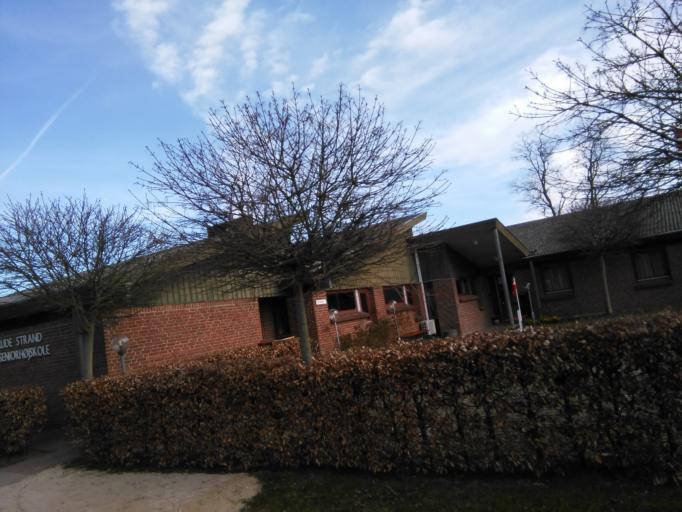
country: DK
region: Central Jutland
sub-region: Arhus Kommune
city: Malling
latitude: 55.9915
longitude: 10.2511
